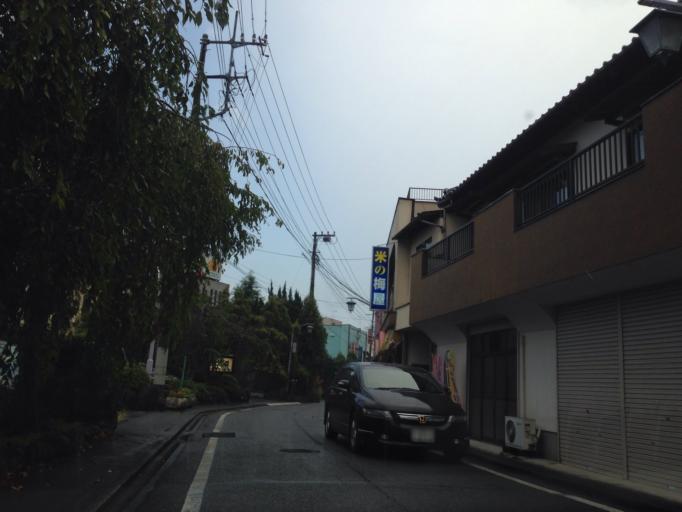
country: JP
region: Shizuoka
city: Mishima
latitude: 35.0368
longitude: 138.9361
